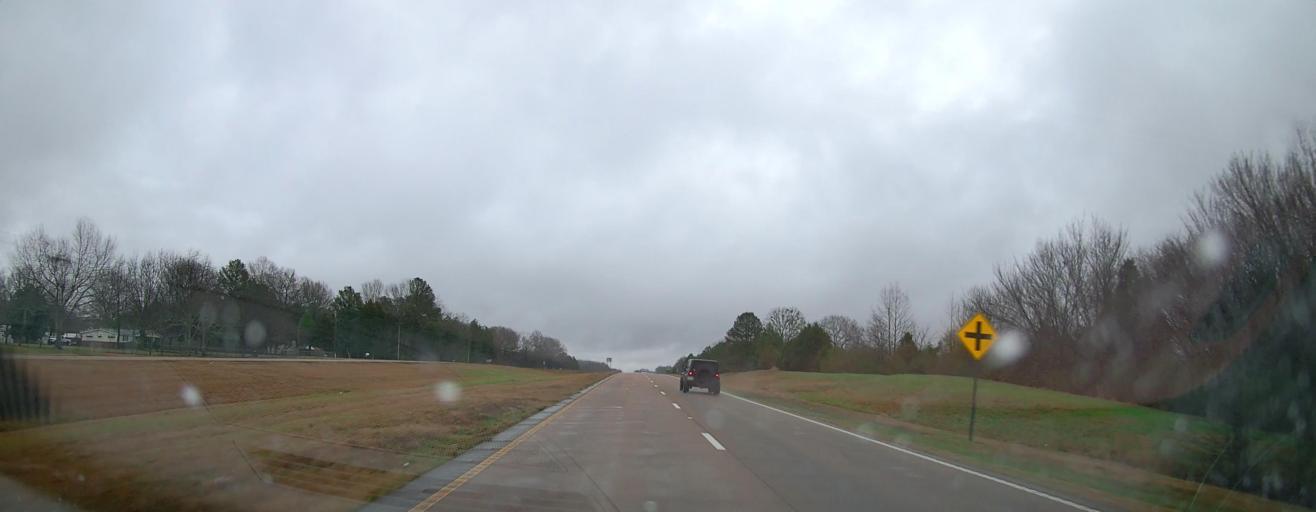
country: US
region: Mississippi
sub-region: Marshall County
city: Holly Springs
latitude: 34.9461
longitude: -89.3555
